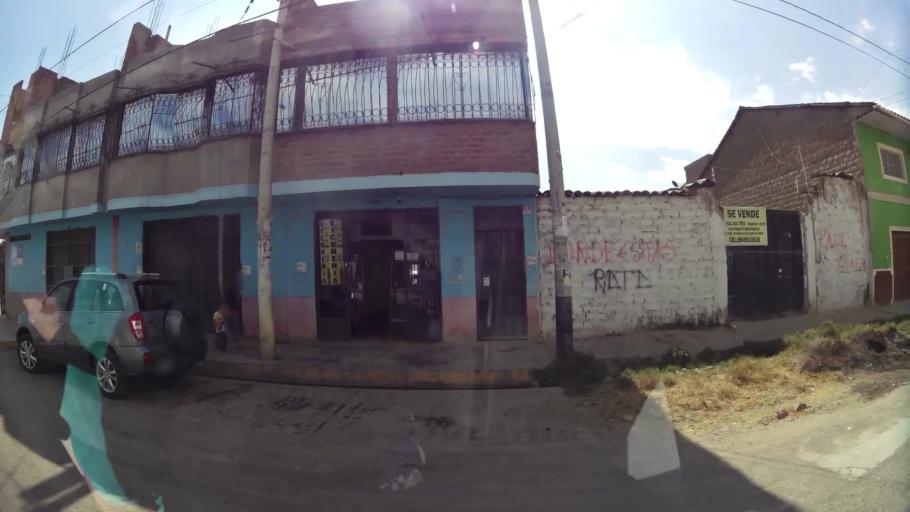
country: PE
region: Junin
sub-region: Provincia de Huancayo
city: Huancayo
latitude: -12.0853
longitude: -75.1985
